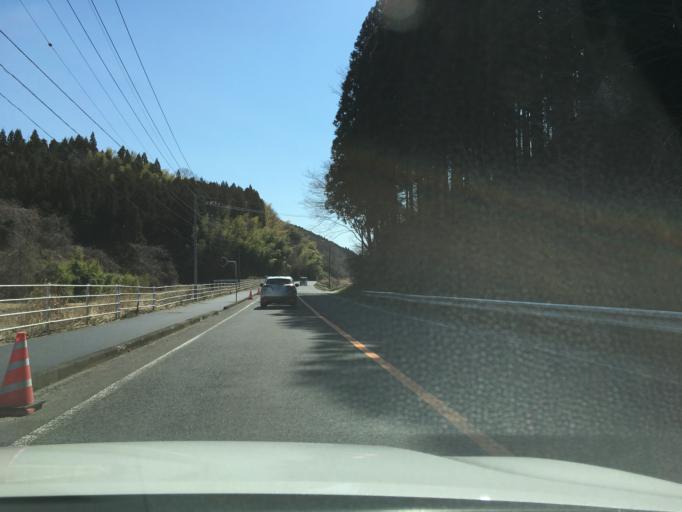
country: JP
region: Tochigi
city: Kuroiso
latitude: 37.0515
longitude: 140.1704
